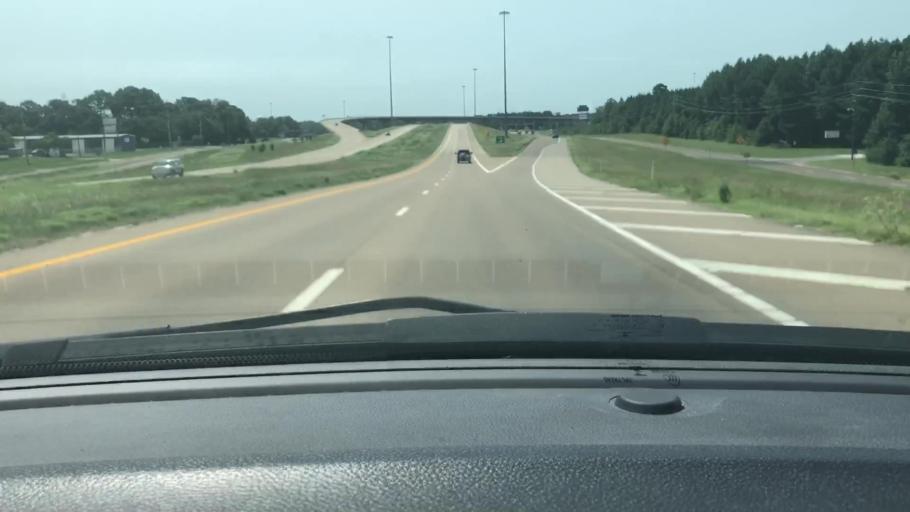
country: US
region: Texas
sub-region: Bowie County
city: Wake Village
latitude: 33.4005
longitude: -94.0980
